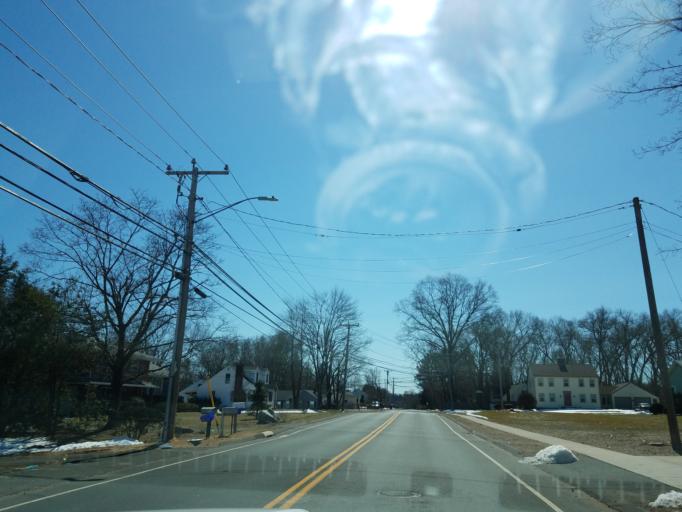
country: US
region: Connecticut
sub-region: Hartford County
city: Windsor Locks
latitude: 41.9122
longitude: -72.6371
